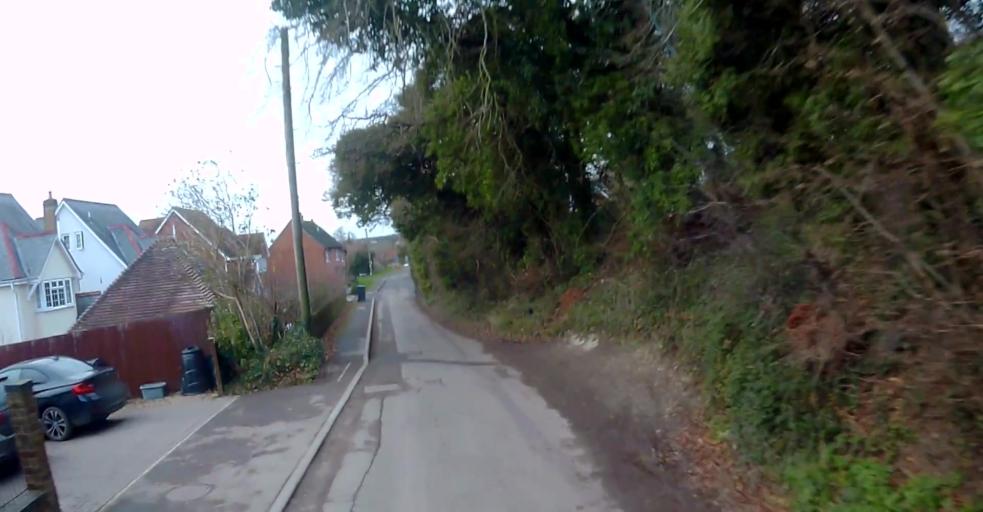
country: GB
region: England
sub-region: Hampshire
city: Overton
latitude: 51.2390
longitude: -1.2572
